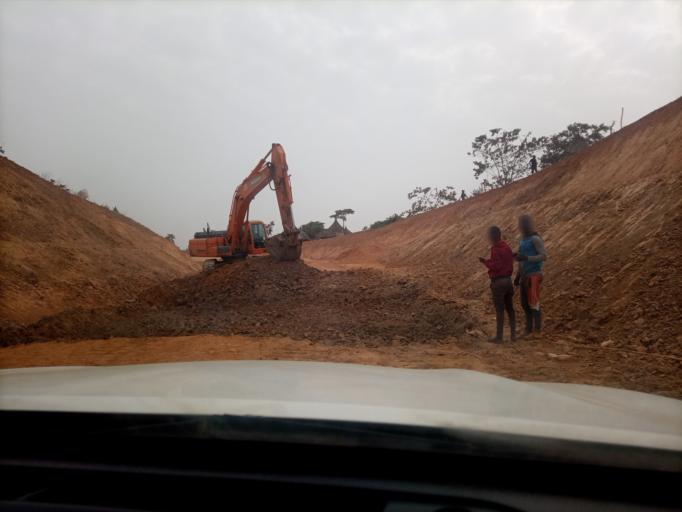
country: ET
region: Oromiya
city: Mendi
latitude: 10.2008
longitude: 35.0696
